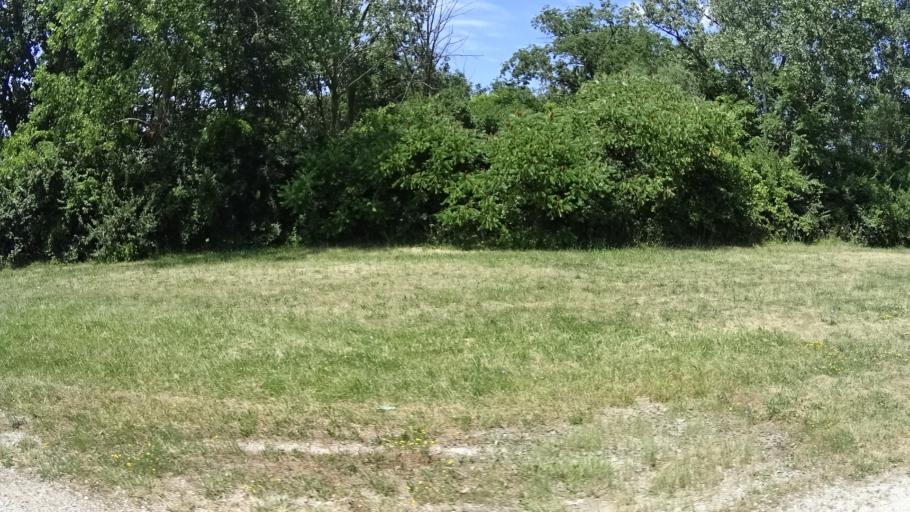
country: US
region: Ohio
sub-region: Erie County
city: Sandusky
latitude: 41.3950
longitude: -82.6554
